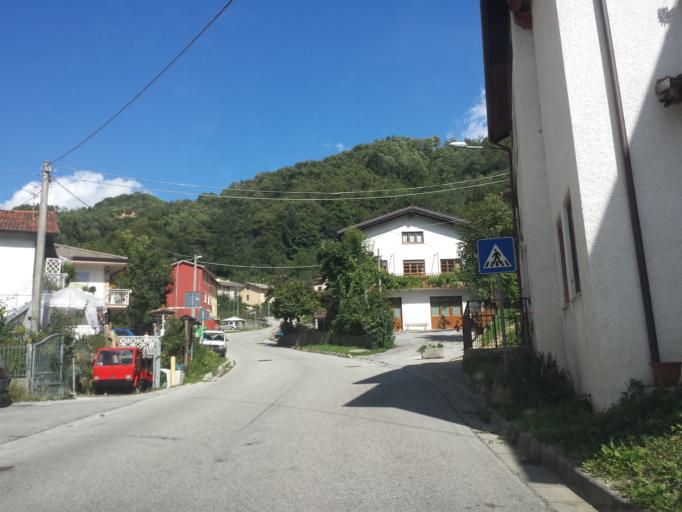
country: IT
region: Veneto
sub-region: Provincia di Vicenza
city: Recoaro Terme
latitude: 45.7068
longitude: 11.2015
